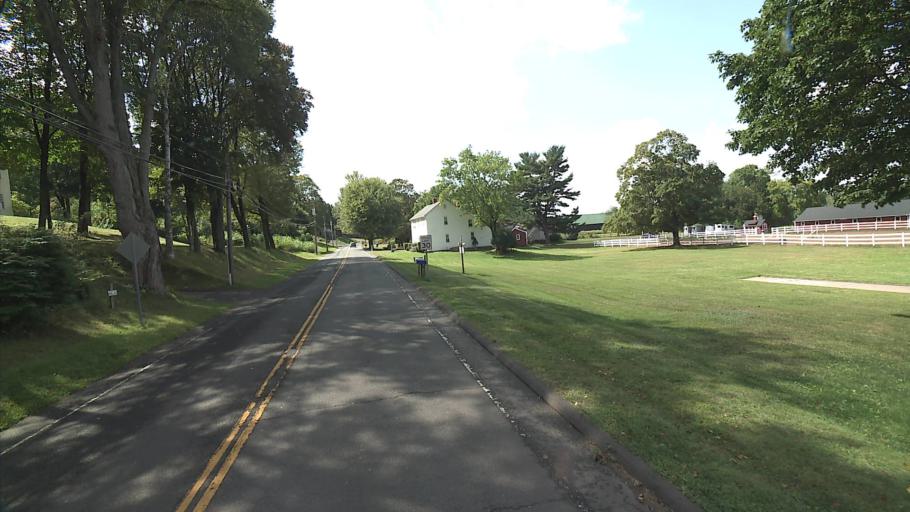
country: US
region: Connecticut
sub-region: Hartford County
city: Glastonbury Center
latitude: 41.6667
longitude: -72.6097
